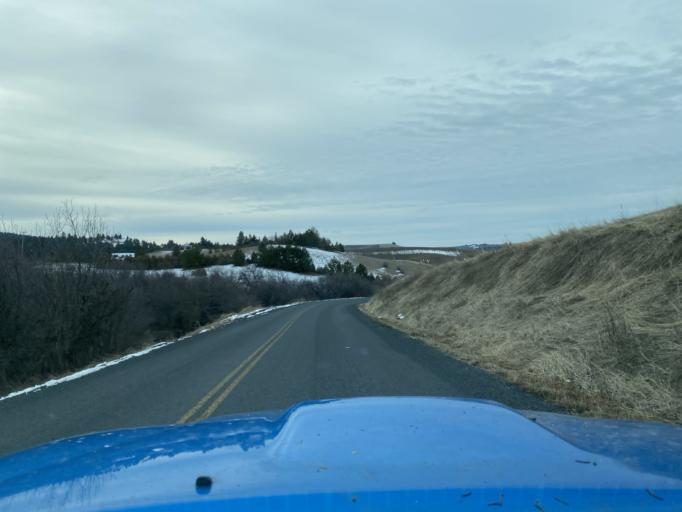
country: US
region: Idaho
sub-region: Latah County
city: Moscow
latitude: 46.7033
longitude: -116.9406
